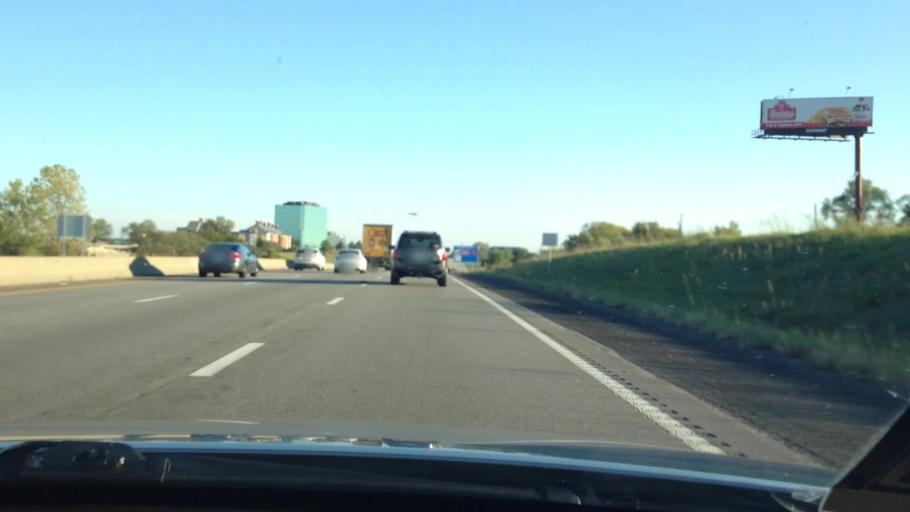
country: US
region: Missouri
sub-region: Platte County
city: Weatherby Lake
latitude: 39.2850
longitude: -94.6780
